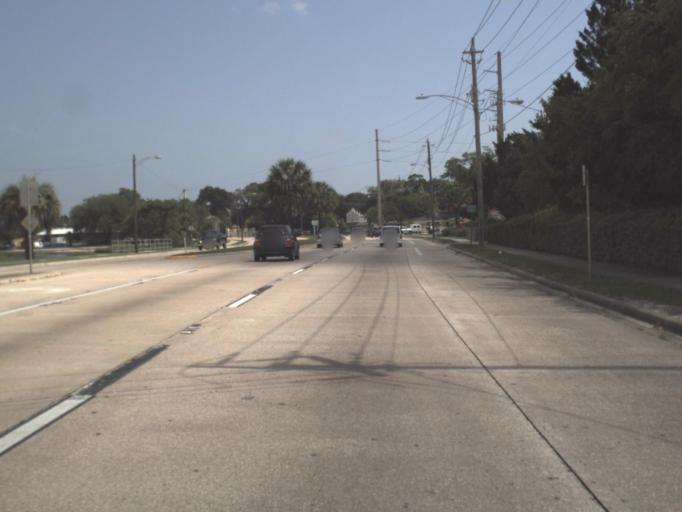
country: US
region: Florida
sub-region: Saint Johns County
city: Saint Augustine
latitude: 29.8846
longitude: -81.3245
